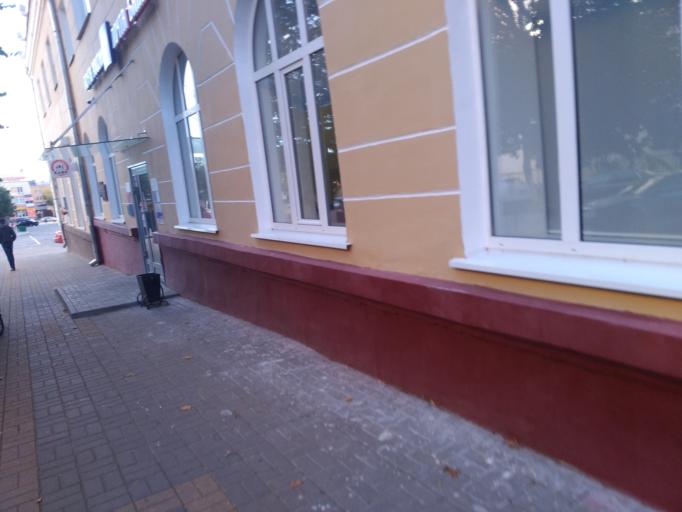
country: RU
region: Kaluga
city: Kaluga
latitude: 54.5159
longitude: 36.2581
